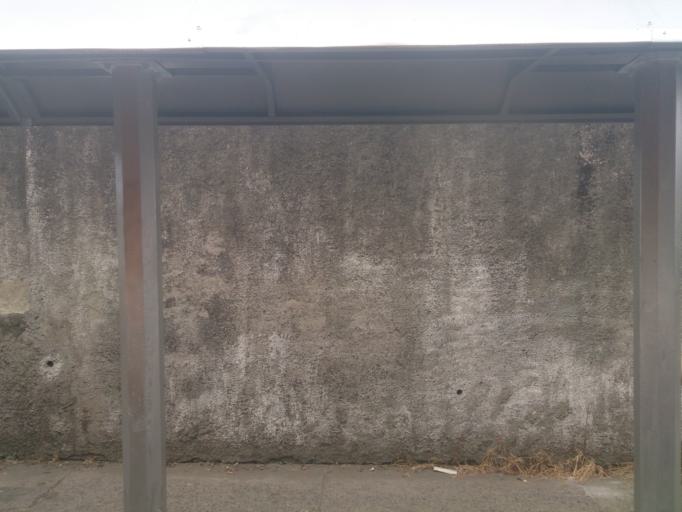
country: CR
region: San Jose
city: San Jose
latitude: 9.9269
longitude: -84.0916
